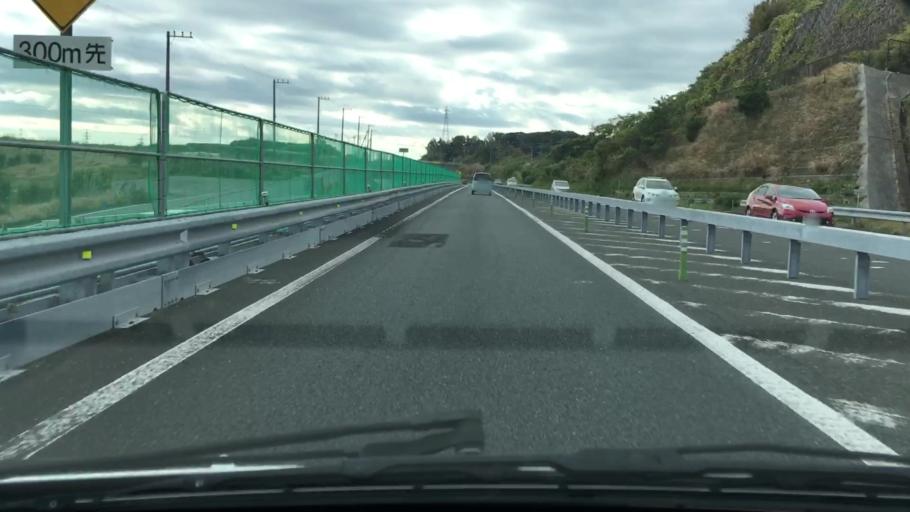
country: JP
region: Chiba
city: Kimitsu
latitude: 35.2443
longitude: 139.8893
